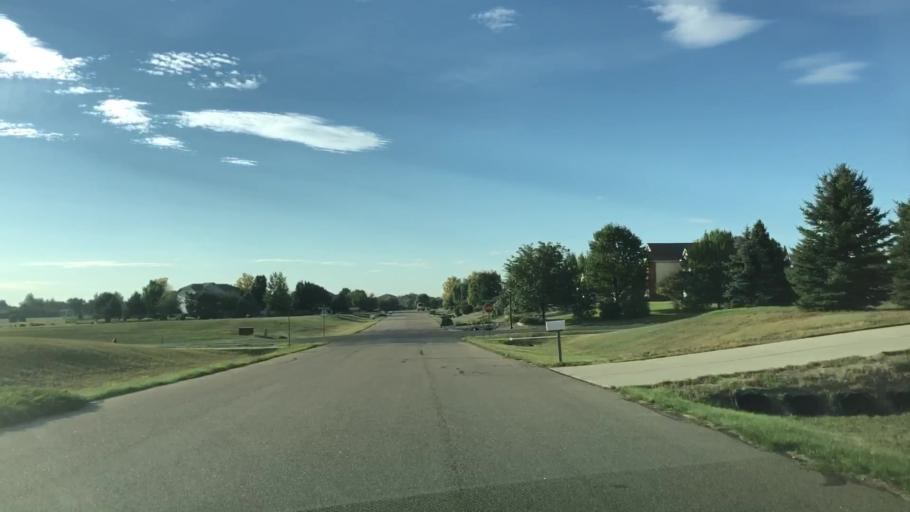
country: US
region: Colorado
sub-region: Weld County
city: Windsor
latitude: 40.4459
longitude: -104.9514
